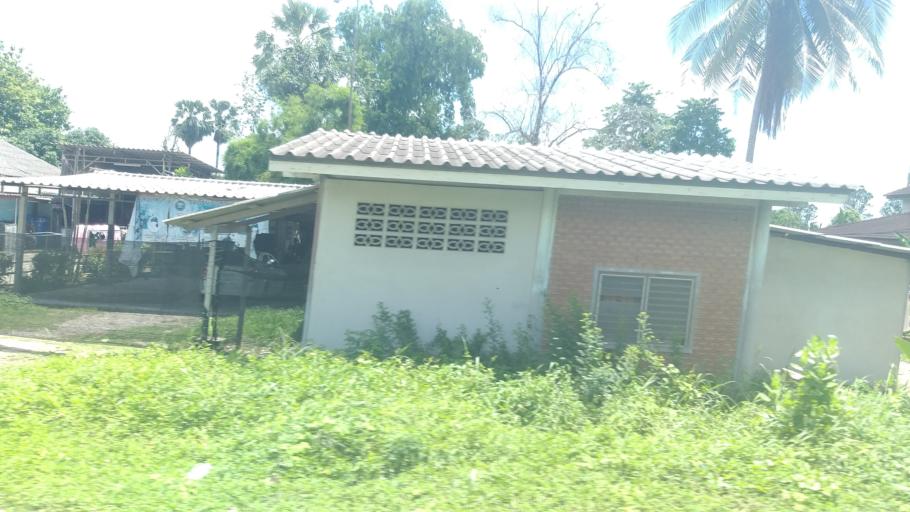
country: TH
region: Nakhon Nayok
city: Ban Na
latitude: 14.2744
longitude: 101.0660
